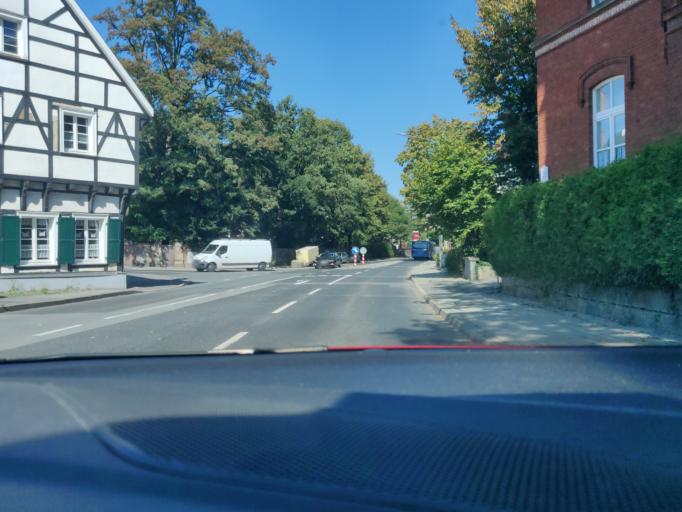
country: DE
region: North Rhine-Westphalia
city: Hattingen
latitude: 51.3527
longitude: 7.1228
